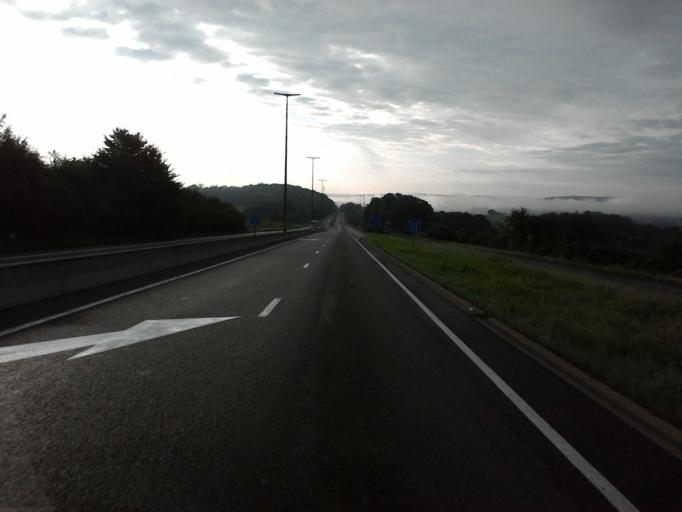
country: BE
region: Wallonia
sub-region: Province du Luxembourg
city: Attert
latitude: 49.7657
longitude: 5.7681
